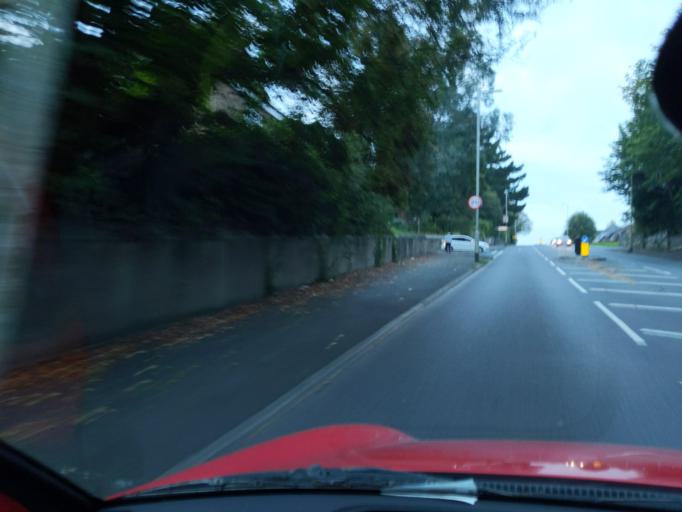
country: GB
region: England
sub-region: Cornwall
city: Millbrook
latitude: 50.3967
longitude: -4.1687
